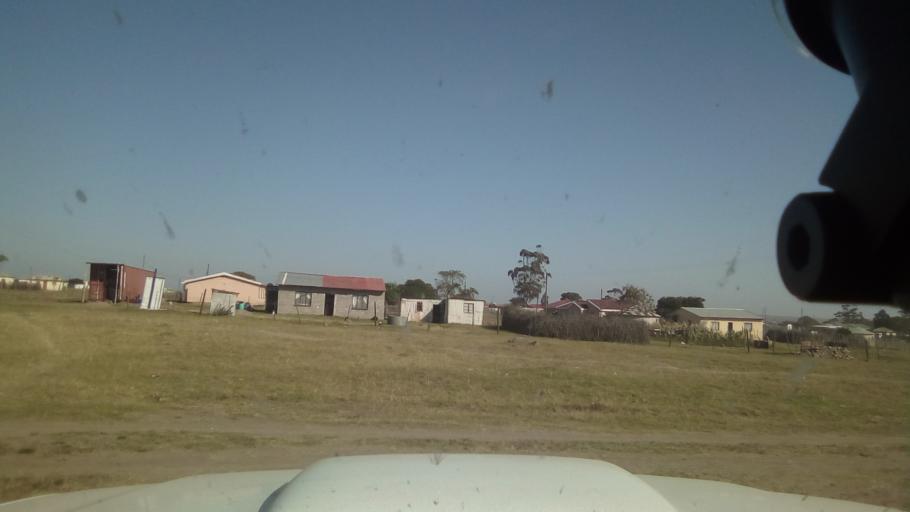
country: ZA
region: Eastern Cape
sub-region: Buffalo City Metropolitan Municipality
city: Bhisho
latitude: -32.9396
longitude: 27.3366
